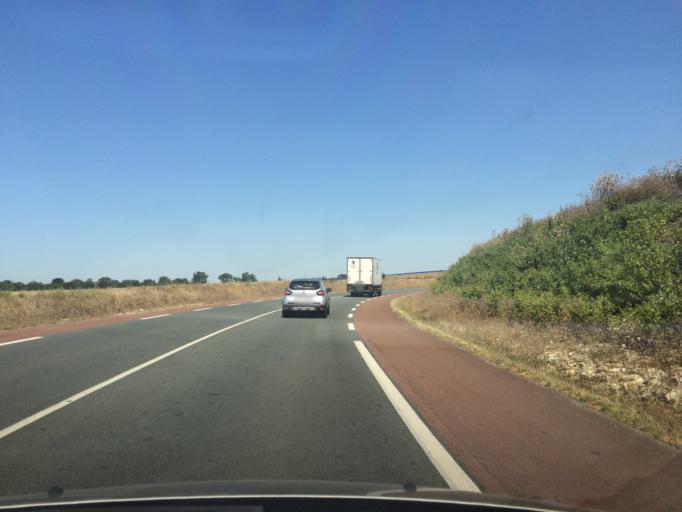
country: FR
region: Poitou-Charentes
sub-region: Departement de la Charente-Maritime
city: Saint-Xandre
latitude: 46.2362
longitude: -1.0770
